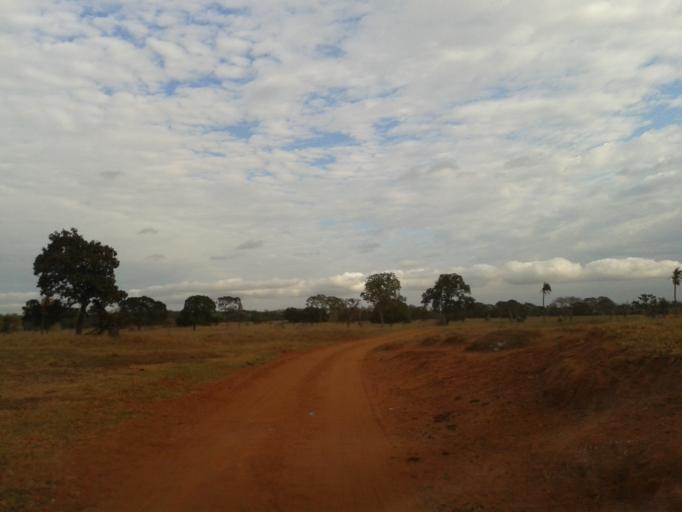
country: BR
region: Minas Gerais
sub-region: Santa Vitoria
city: Santa Vitoria
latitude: -18.7503
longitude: -50.2063
